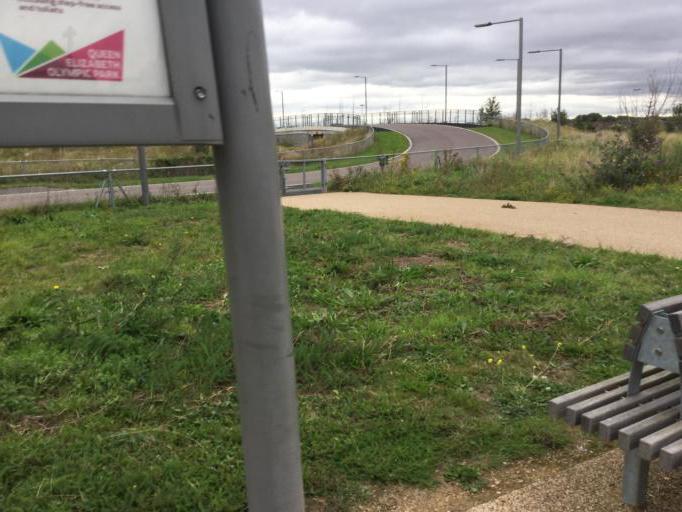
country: GB
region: England
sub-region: Greater London
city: Hackney
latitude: 51.5507
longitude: -0.0120
